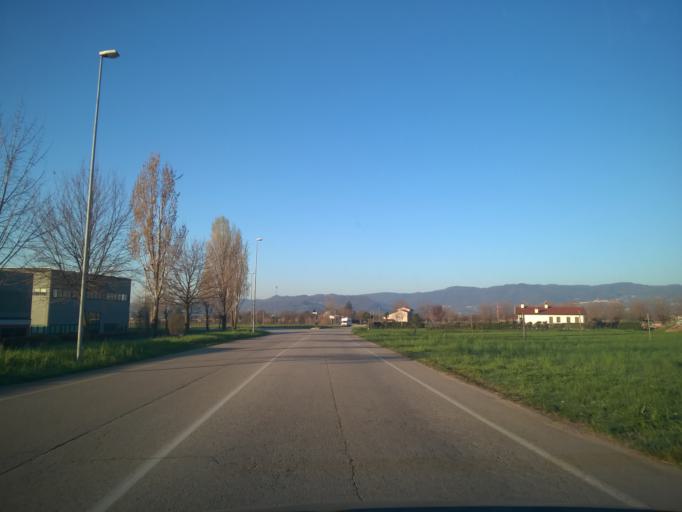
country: IT
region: Veneto
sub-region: Provincia di Vicenza
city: Thiene
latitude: 45.6898
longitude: 11.4615
